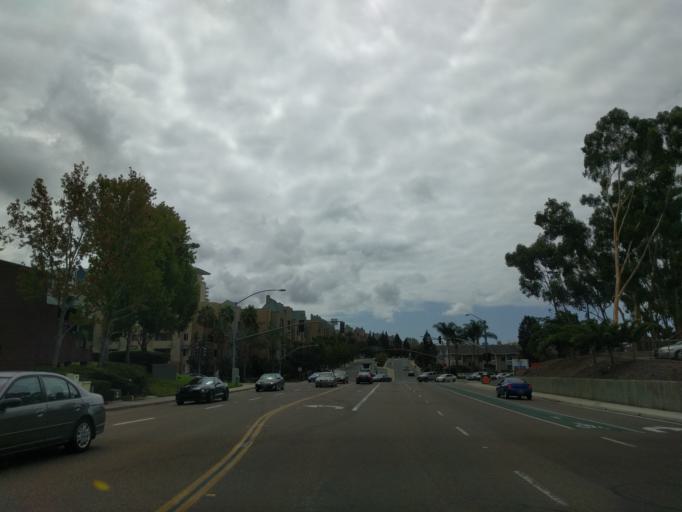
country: US
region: California
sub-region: San Diego County
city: La Jolla
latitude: 32.8723
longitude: -117.2184
